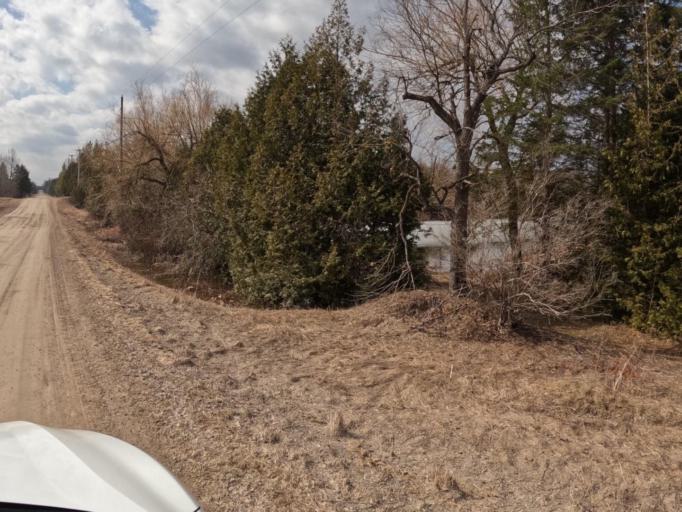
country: CA
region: Ontario
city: Orangeville
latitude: 43.9039
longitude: -80.2361
